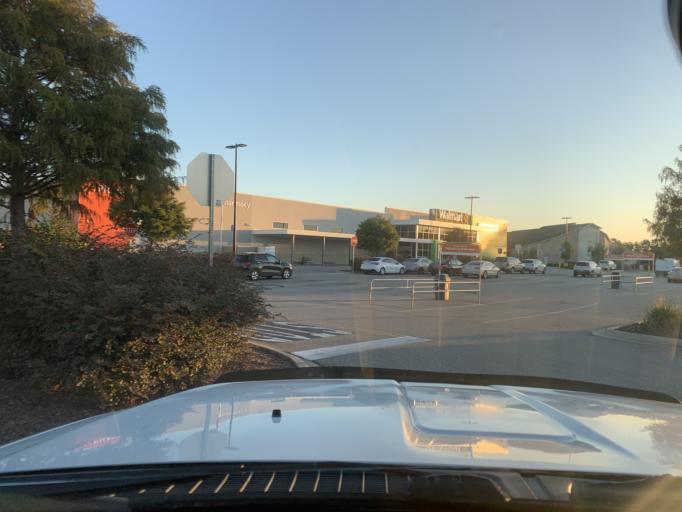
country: US
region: Texas
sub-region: Fort Bend County
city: Meadows Place
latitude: 29.6514
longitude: -95.6178
